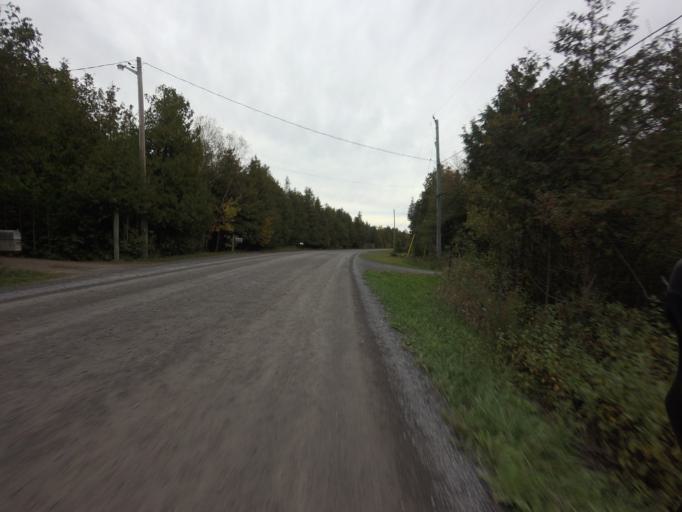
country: CA
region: Ontario
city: Bells Corners
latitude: 45.0673
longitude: -75.7610
